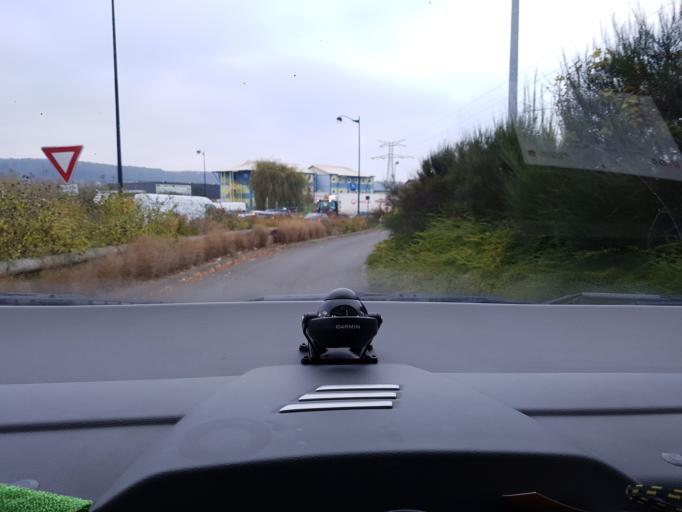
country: FR
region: Haute-Normandie
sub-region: Departement de la Seine-Maritime
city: Eu
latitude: 50.0606
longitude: 1.4099
